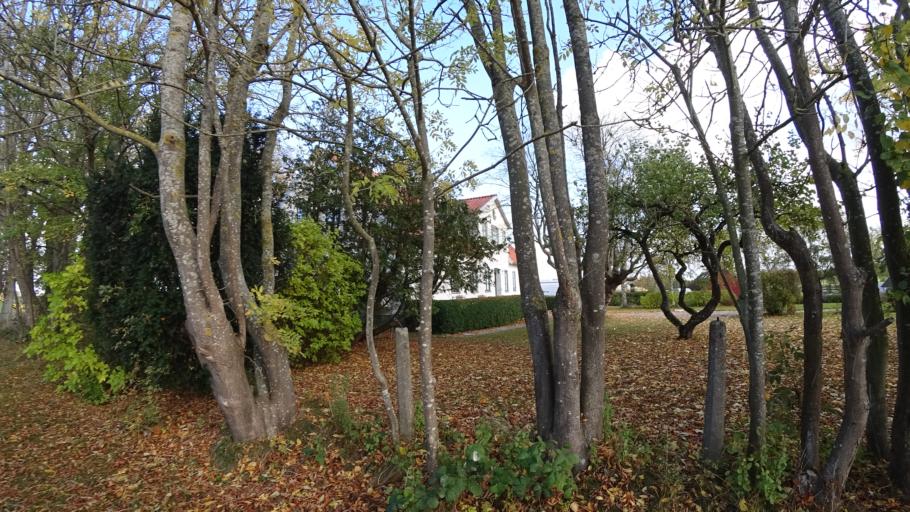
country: SE
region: Skane
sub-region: Staffanstorps Kommun
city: Hjaerup
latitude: 55.6301
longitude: 13.1462
